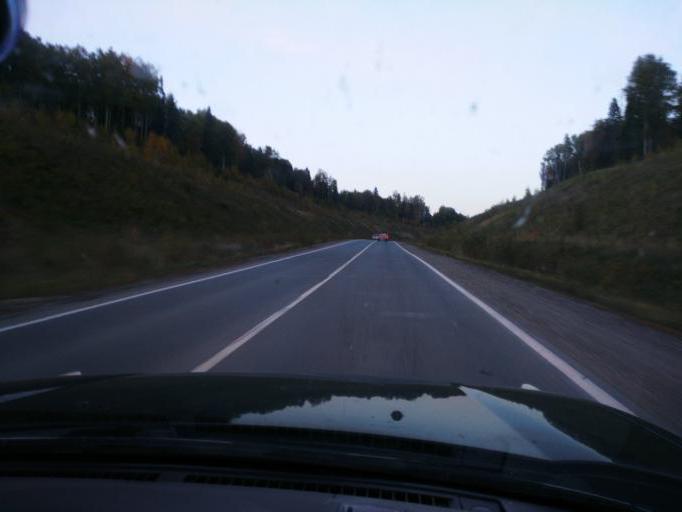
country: RU
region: Perm
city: Sylva
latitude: 58.2954
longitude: 56.8086
